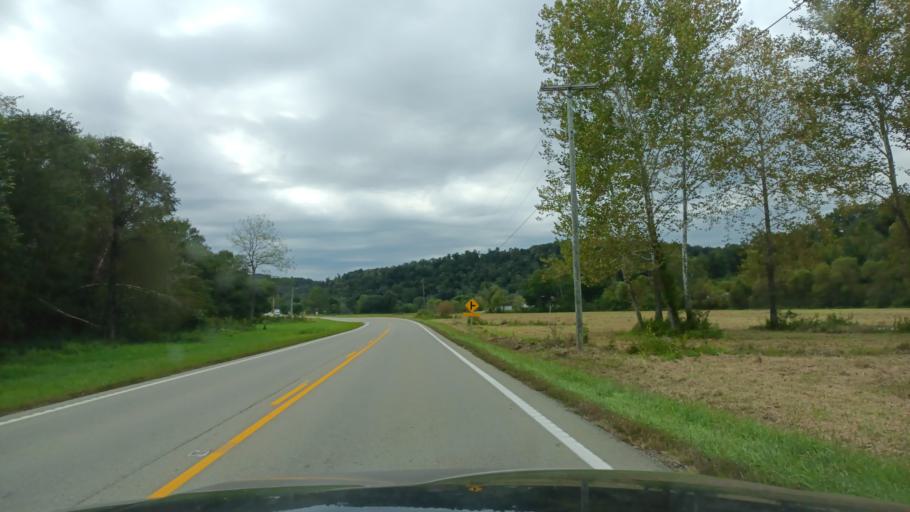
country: US
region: Ohio
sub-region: Vinton County
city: McArthur
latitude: 39.2747
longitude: -82.6185
